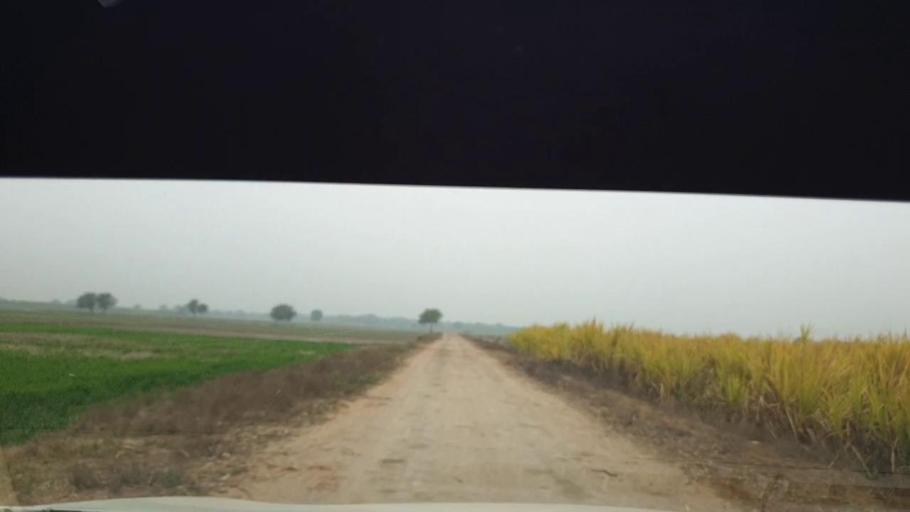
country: PK
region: Sindh
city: Berani
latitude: 25.7510
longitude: 68.7567
